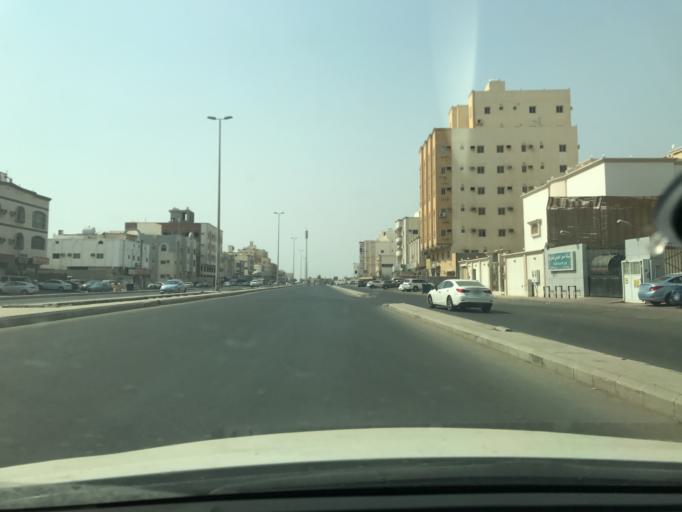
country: SA
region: Makkah
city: Jeddah
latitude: 21.6255
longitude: 39.1684
